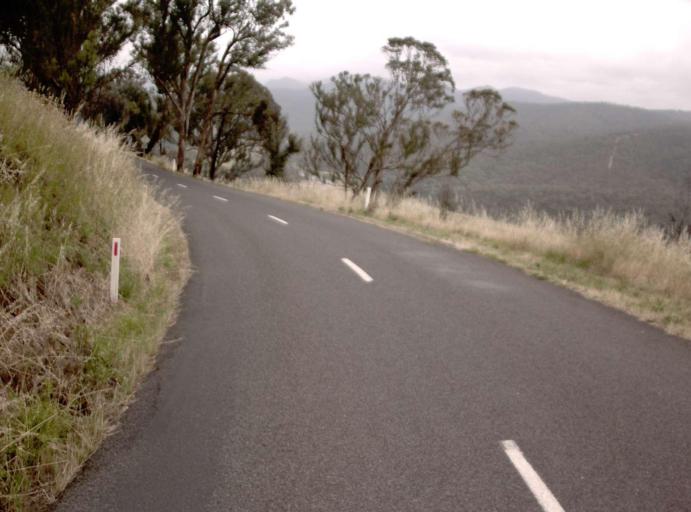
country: AU
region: Victoria
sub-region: Wellington
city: Heyfield
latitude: -37.8225
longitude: 146.6755
